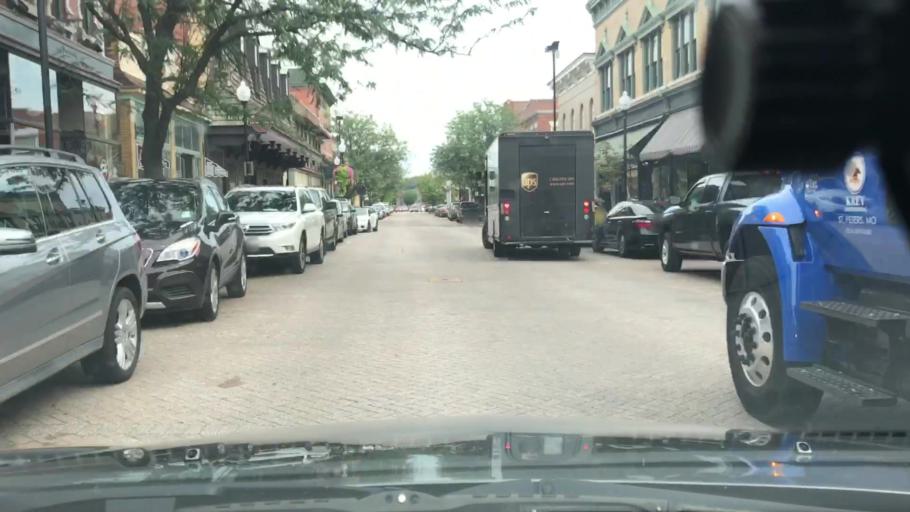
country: US
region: Missouri
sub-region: Saint Charles County
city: Saint Charles
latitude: 38.7825
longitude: -90.4807
